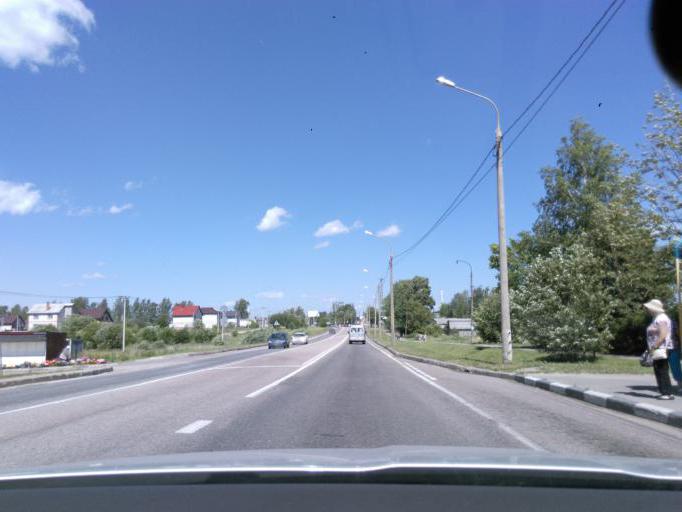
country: RU
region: Moskovskaya
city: Solnechnogorsk
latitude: 56.1744
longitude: 36.9502
